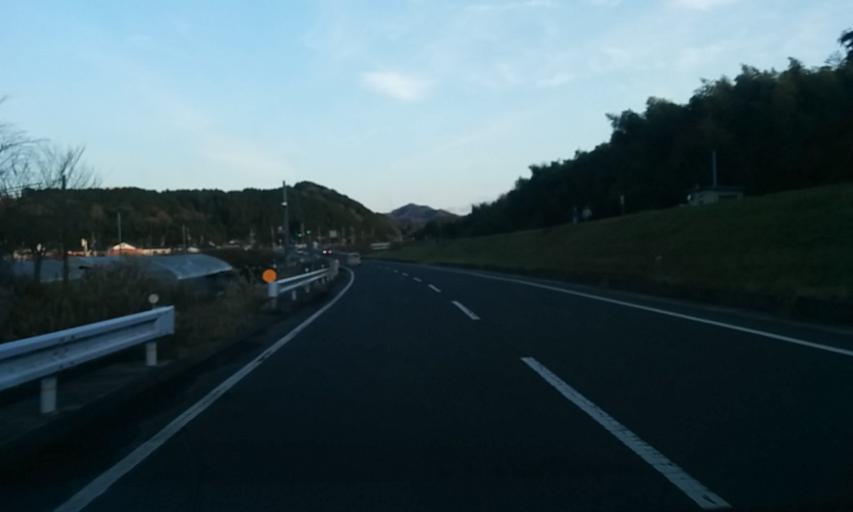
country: JP
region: Kyoto
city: Ayabe
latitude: 35.3118
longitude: 135.2563
